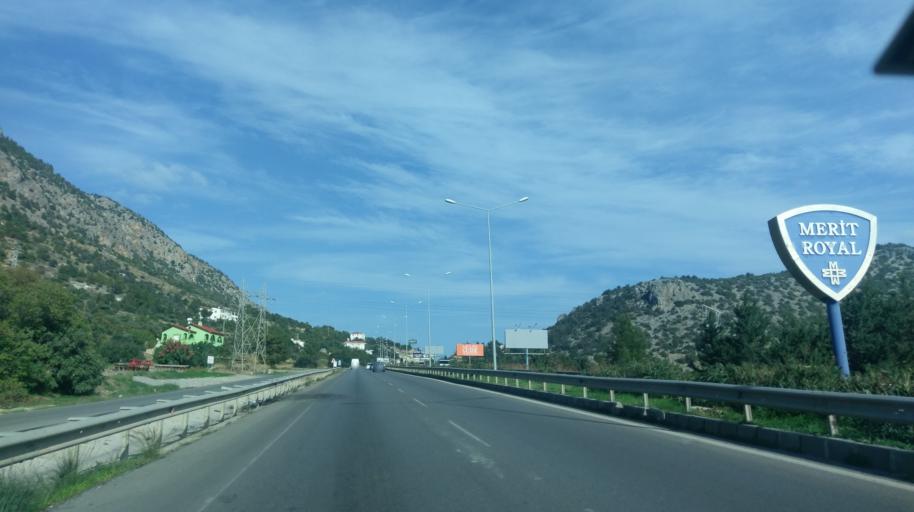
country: CY
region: Keryneia
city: Kyrenia
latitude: 35.2980
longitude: 33.2809
